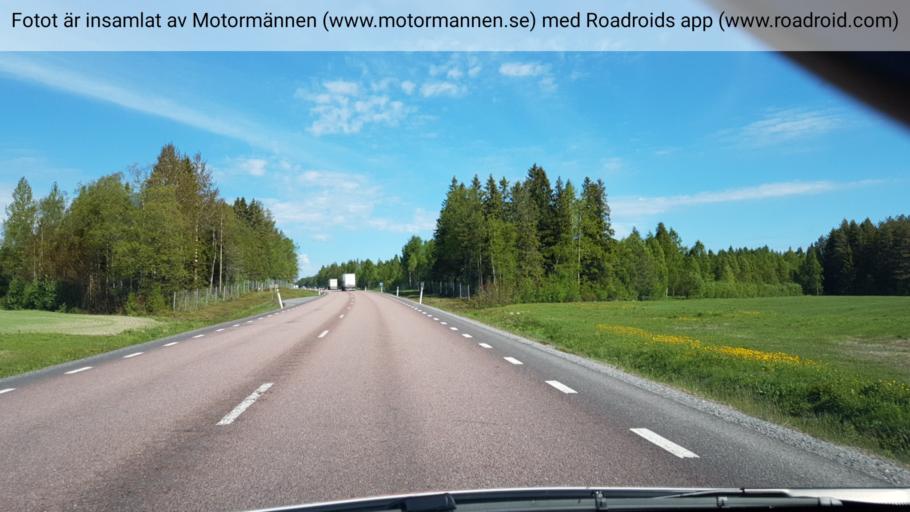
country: SE
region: Vaesterbotten
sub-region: Skelleftea Kommun
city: Burea
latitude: 64.4044
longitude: 21.3003
